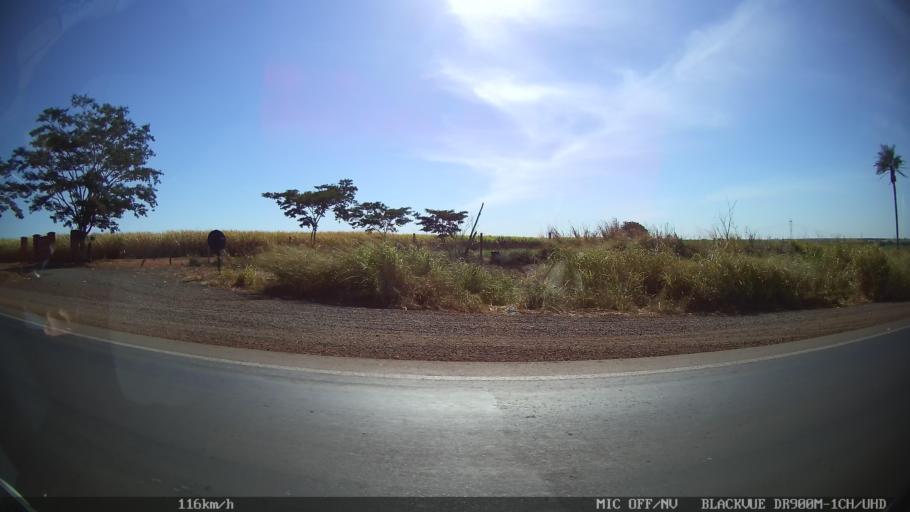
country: BR
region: Sao Paulo
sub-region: Olimpia
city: Olimpia
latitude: -20.6363
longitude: -48.8202
